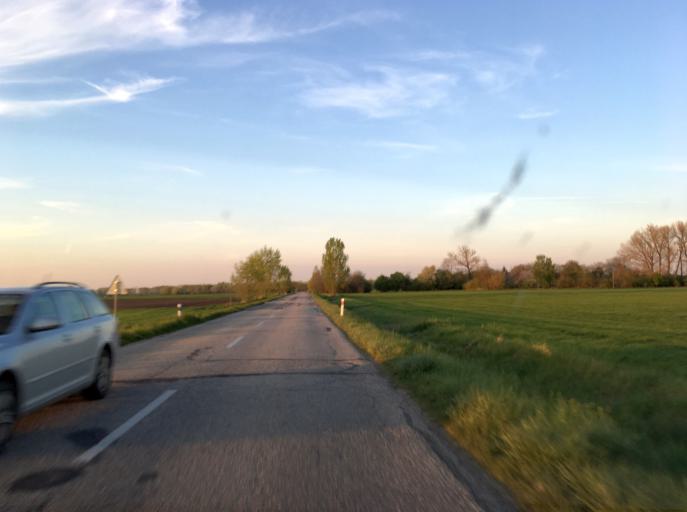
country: SK
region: Nitriansky
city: Kolarovo
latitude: 47.8798
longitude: 17.9191
